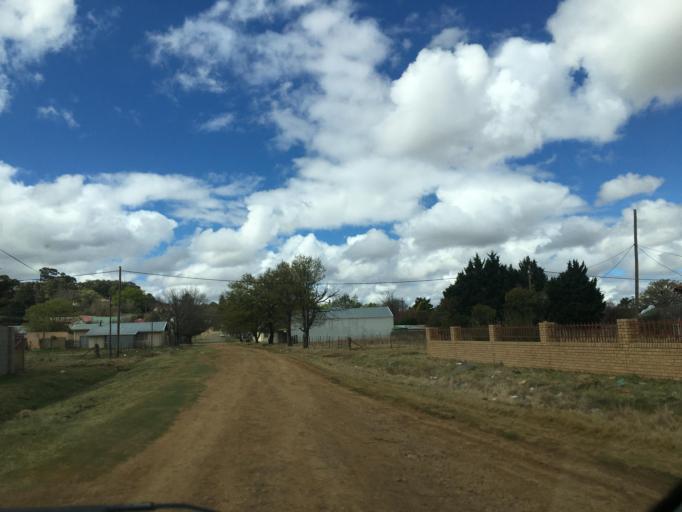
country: ZA
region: Eastern Cape
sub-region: Chris Hani District Municipality
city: Elliot
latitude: -31.3314
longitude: 27.8441
